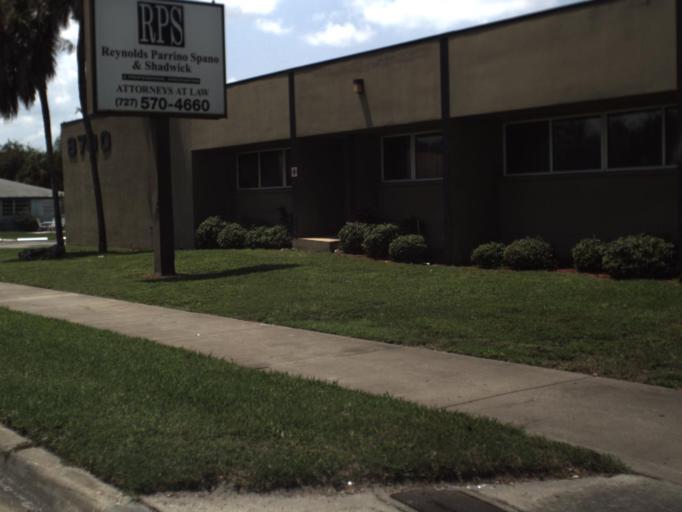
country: US
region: Florida
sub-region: Pinellas County
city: Gandy
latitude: 27.8521
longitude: -82.6389
